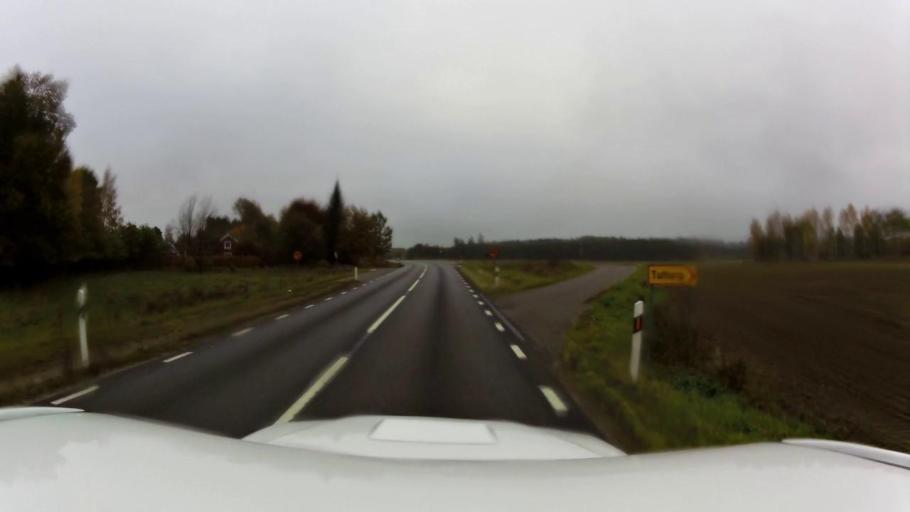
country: SE
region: OEstergoetland
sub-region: Linkopings Kommun
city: Linghem
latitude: 58.3854
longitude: 15.7854
